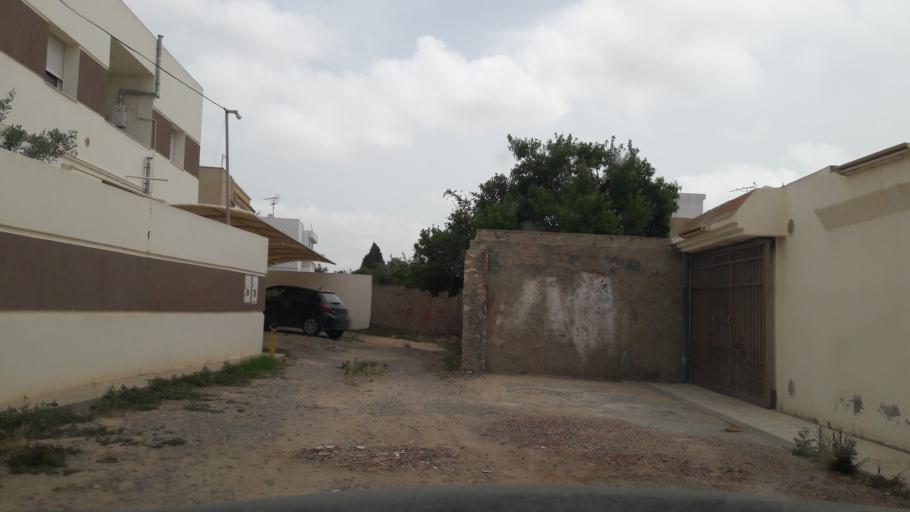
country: TN
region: Safaqis
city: Sfax
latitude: 34.7722
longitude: 10.7564
